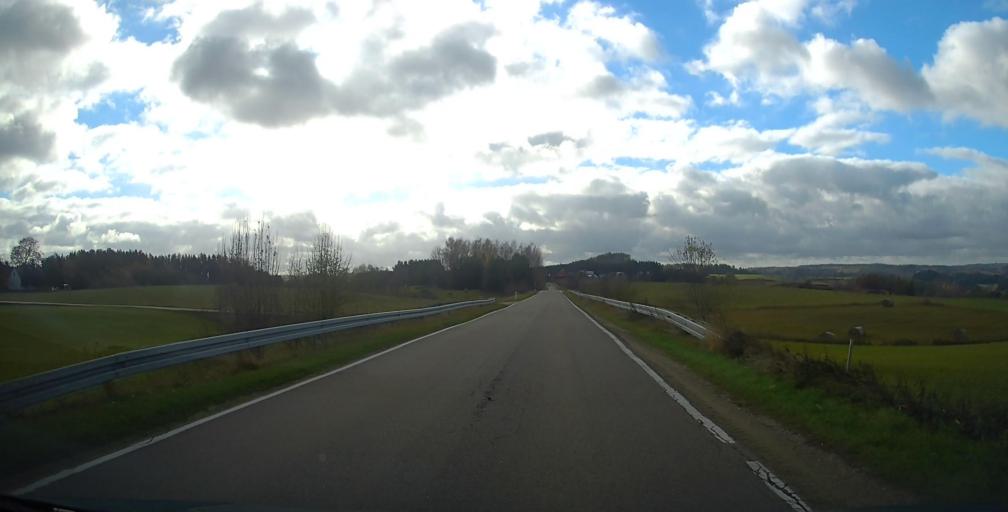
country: PL
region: Podlasie
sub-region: Suwalki
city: Suwalki
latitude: 54.2619
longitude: 22.9200
